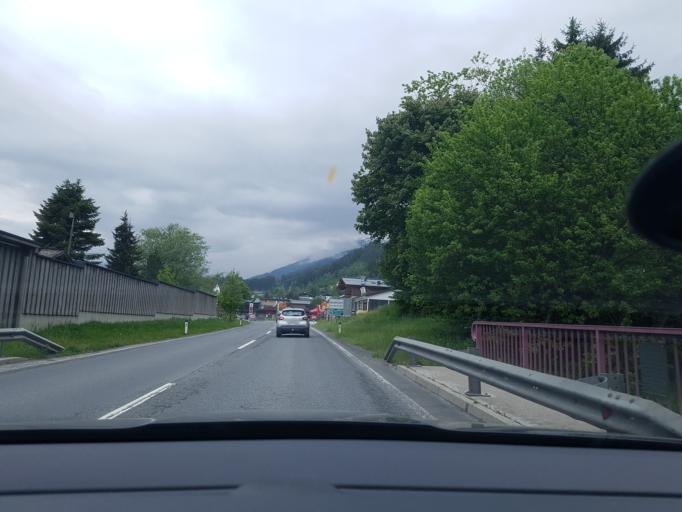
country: AT
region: Salzburg
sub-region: Politischer Bezirk Zell am See
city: Neukirchen am Grossvenediger
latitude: 47.2547
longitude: 12.2860
